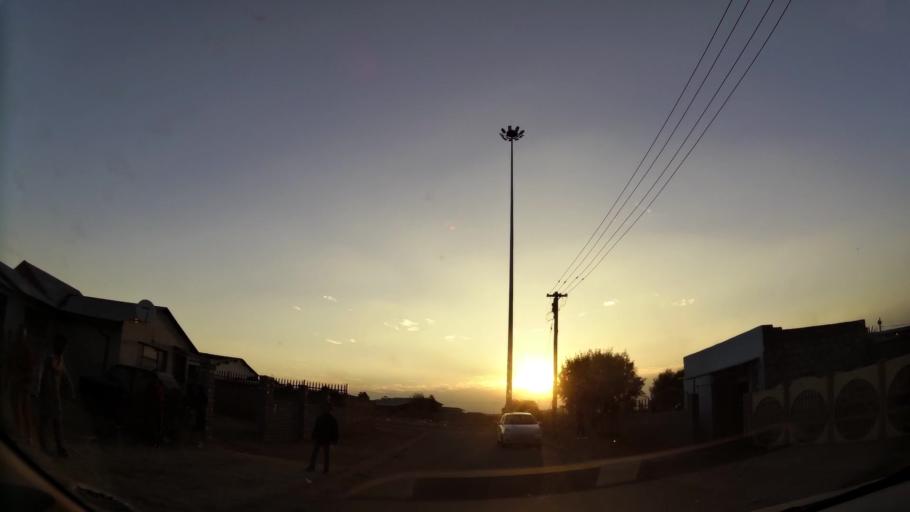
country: ZA
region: Gauteng
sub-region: West Rand District Municipality
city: Randfontein
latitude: -26.2009
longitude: 27.7100
